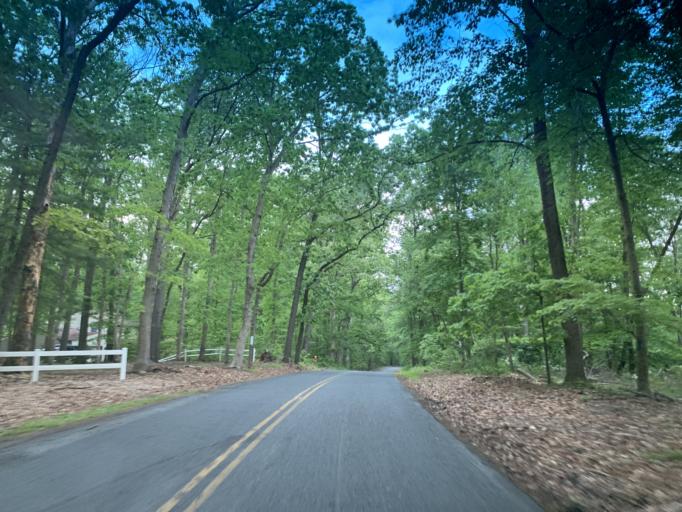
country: US
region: Pennsylvania
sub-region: York County
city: Susquehanna Trails
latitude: 39.6881
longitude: -76.2867
